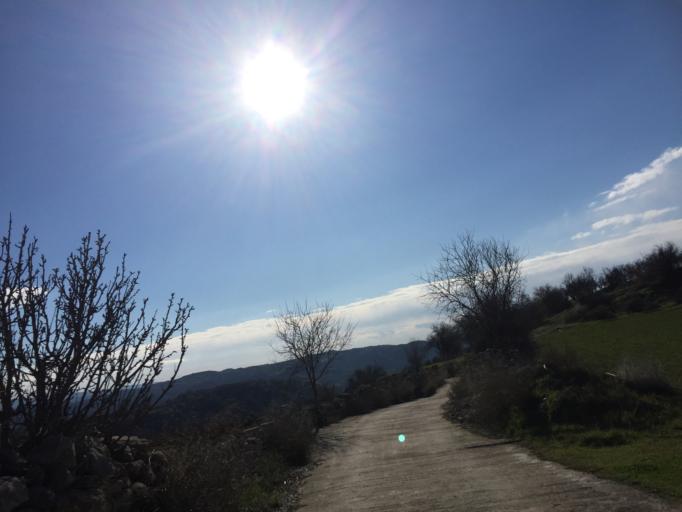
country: CY
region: Pafos
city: Mesogi
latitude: 34.8384
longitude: 32.5103
